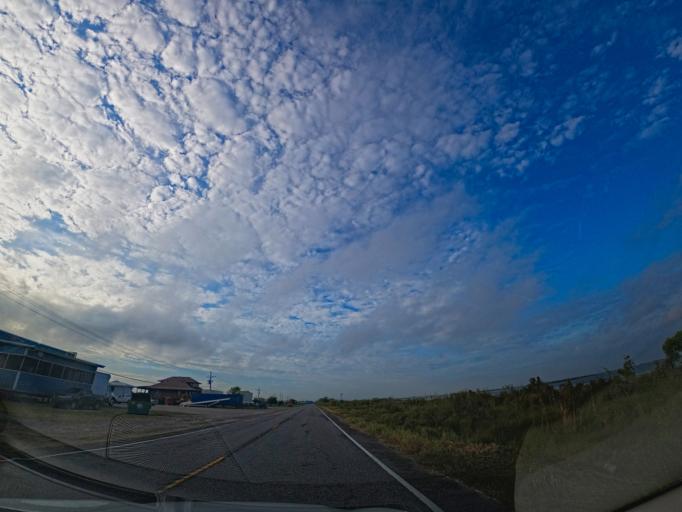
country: US
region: Louisiana
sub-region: Terrebonne Parish
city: Chauvin
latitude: 29.3607
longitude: -90.6260
